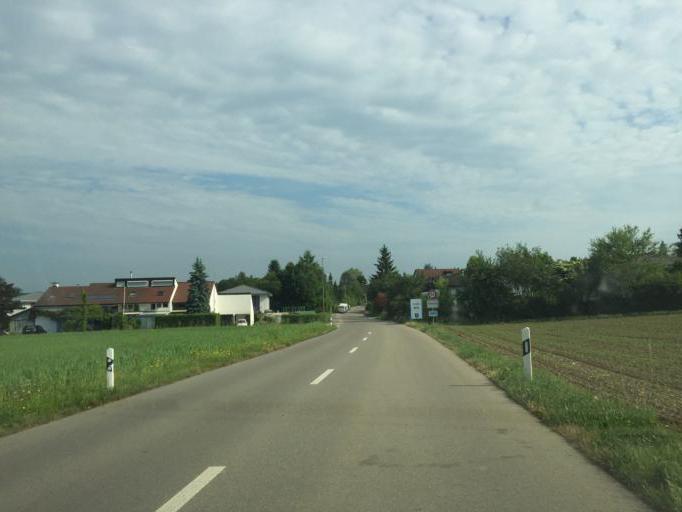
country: DE
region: Baden-Wuerttemberg
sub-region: Freiburg Region
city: Lottstetten
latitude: 47.6337
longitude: 8.6003
